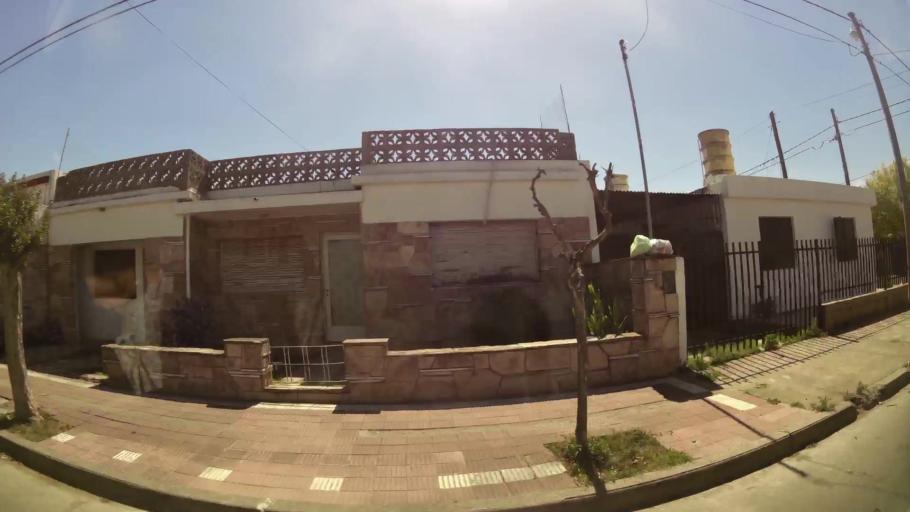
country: AR
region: Cordoba
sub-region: Departamento de Capital
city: Cordoba
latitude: -31.3753
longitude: -64.1372
